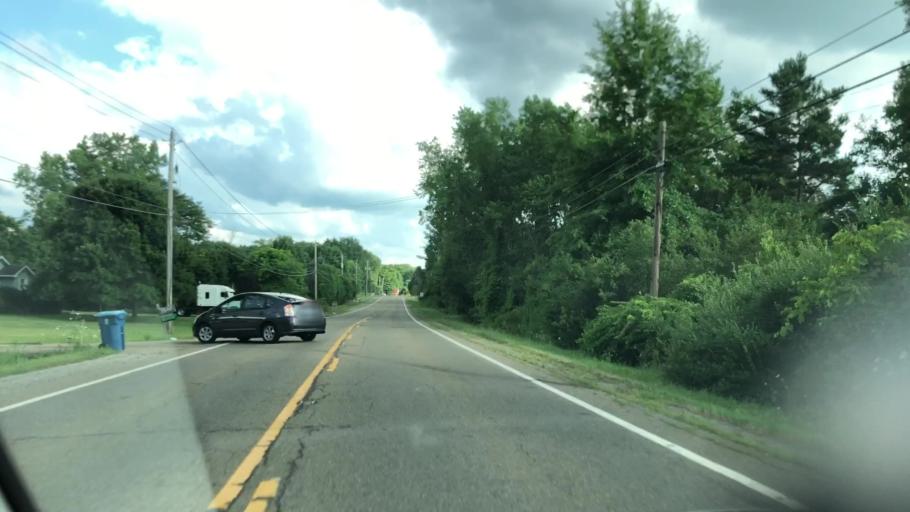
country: US
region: Ohio
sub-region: Summit County
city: Norton
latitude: 41.0792
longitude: -81.6415
